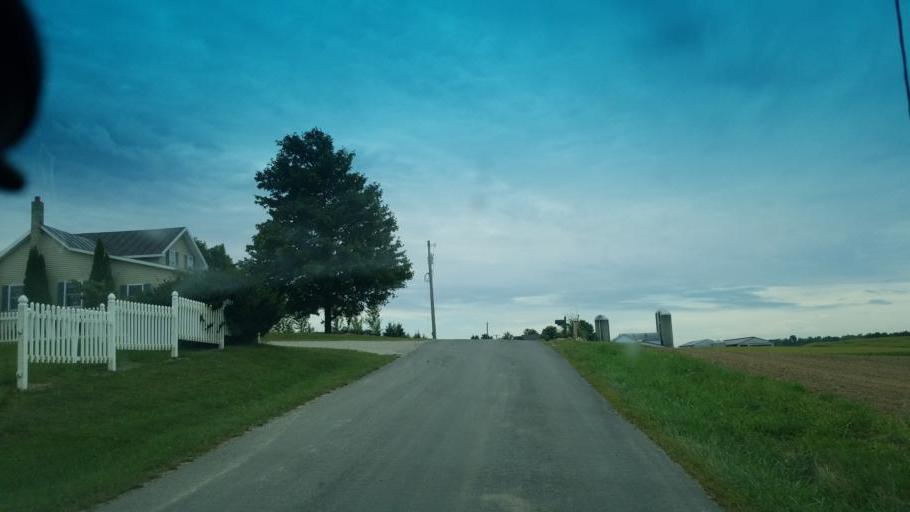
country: US
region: Ohio
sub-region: Huron County
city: Greenwich
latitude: 40.9375
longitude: -82.5091
